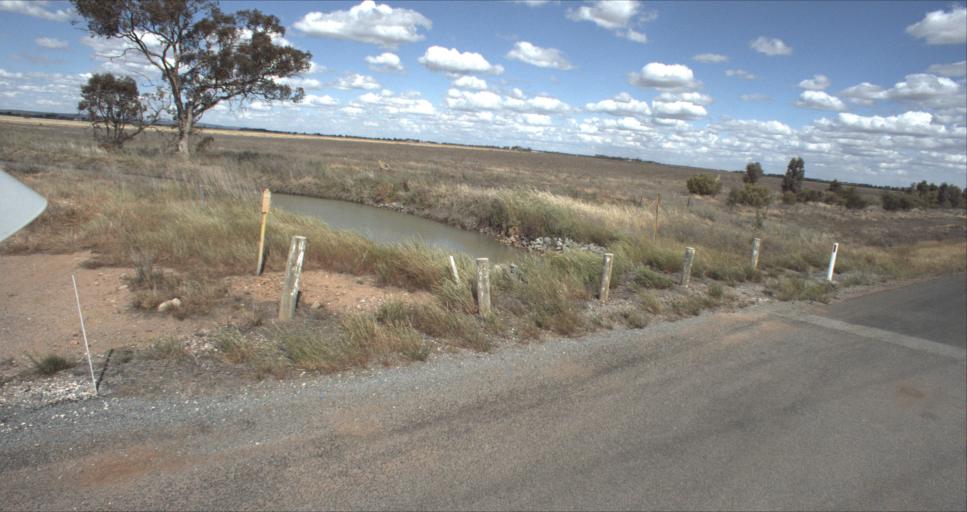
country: AU
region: New South Wales
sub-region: Leeton
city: Leeton
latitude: -34.4279
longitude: 146.2584
